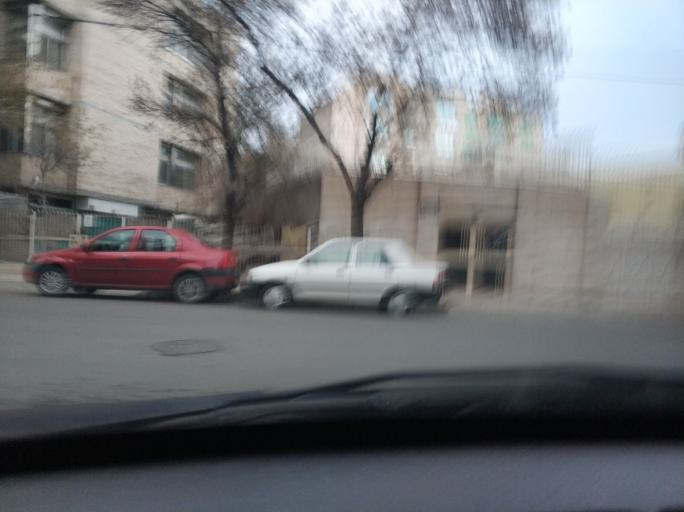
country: IR
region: Razavi Khorasan
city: Mashhad
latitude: 36.2756
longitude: 59.5941
